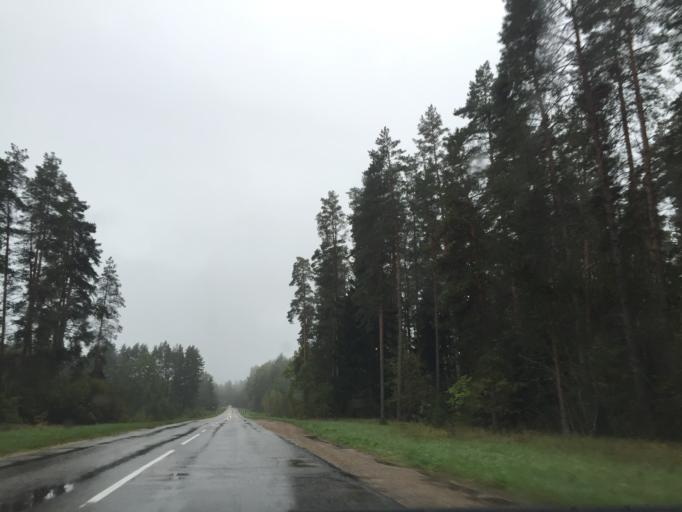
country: LV
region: Incukalns
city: Incukalns
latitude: 57.0309
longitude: 24.6828
